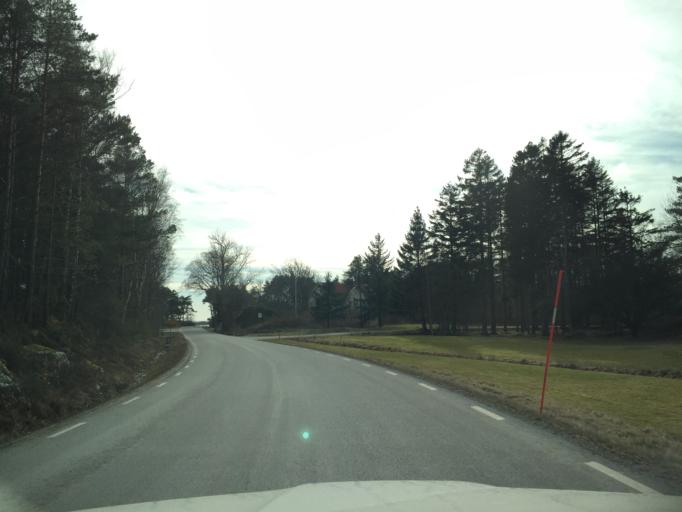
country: SE
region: Vaestra Goetaland
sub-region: Tjorns Kommun
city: Skaerhamn
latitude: 58.0259
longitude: 11.5367
